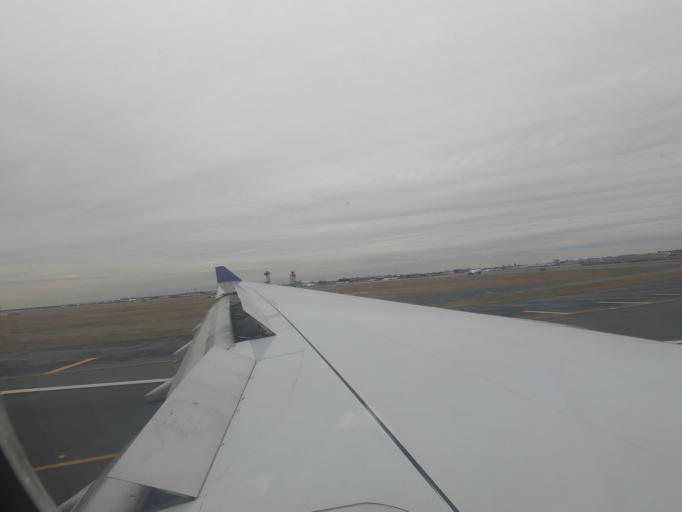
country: US
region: New York
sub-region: Nassau County
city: Inwood
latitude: 40.6380
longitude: -73.7607
